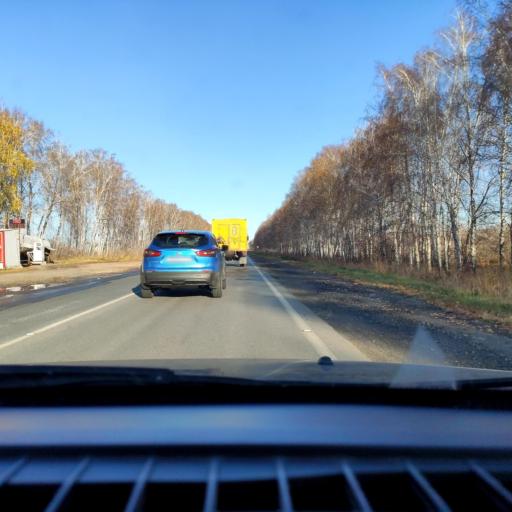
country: RU
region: Samara
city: Tol'yatti
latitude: 53.5916
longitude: 49.3286
